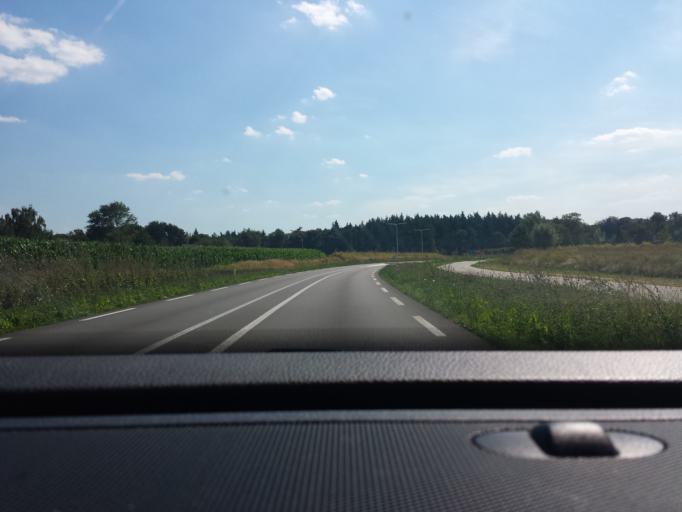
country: NL
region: Gelderland
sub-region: Gemeente Bronckhorst
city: Baak
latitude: 52.0060
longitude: 6.2292
